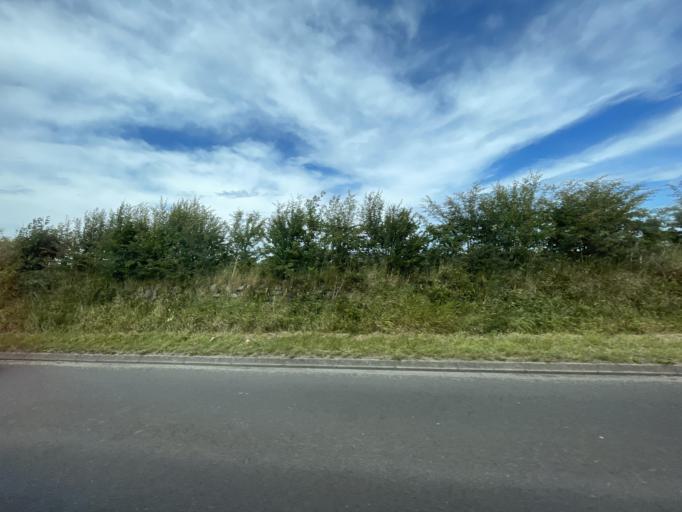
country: GB
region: Wales
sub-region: Anglesey
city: Llanfairpwllgwyngyll
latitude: 53.2223
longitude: -4.2212
